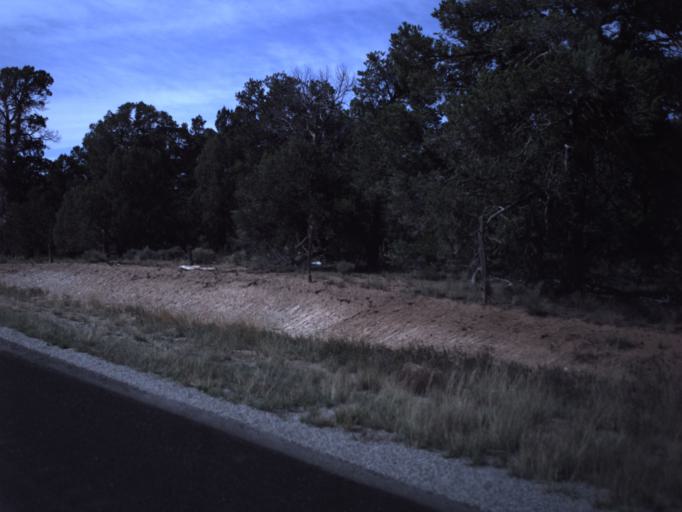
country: US
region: Utah
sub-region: San Juan County
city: Monticello
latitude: 37.8565
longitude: -109.1922
